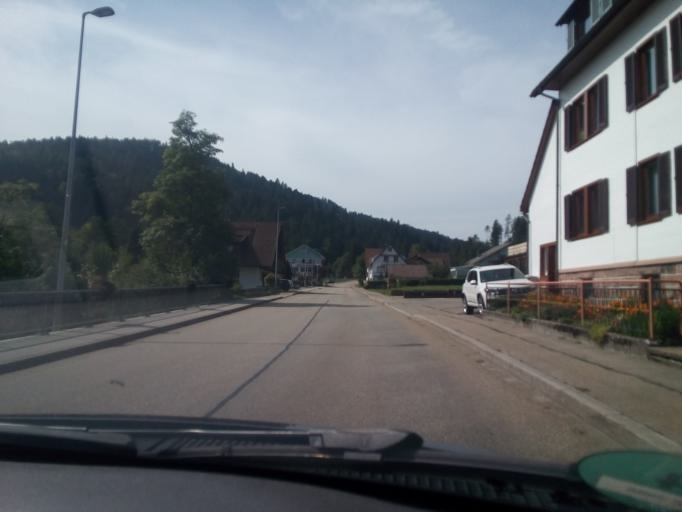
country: DE
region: Baden-Wuerttemberg
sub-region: Karlsruhe Region
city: Biberach
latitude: 48.5355
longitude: 8.2869
